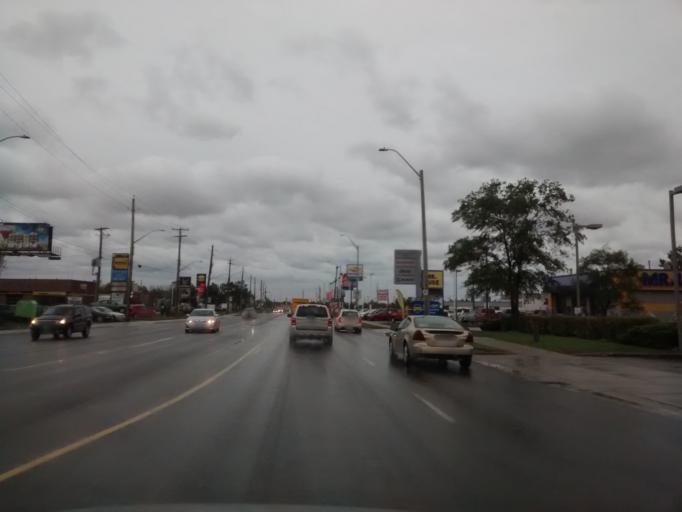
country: CA
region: Ontario
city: Hamilton
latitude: 43.2373
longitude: -79.7603
